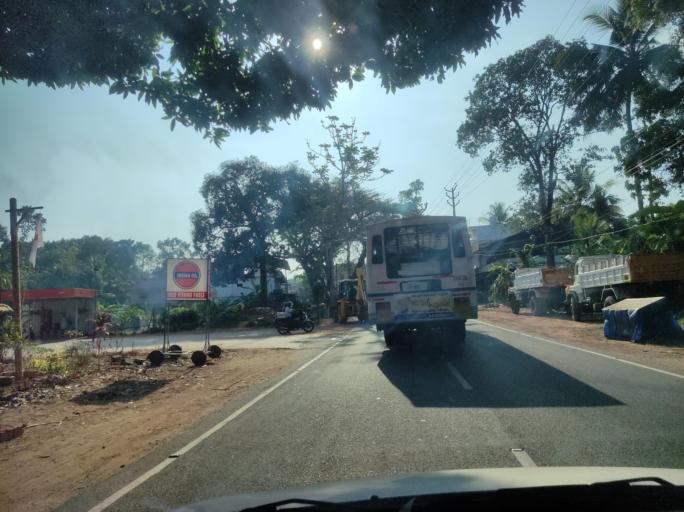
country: IN
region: Kerala
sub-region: Alappuzha
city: Kattanam
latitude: 9.1712
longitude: 76.5995
